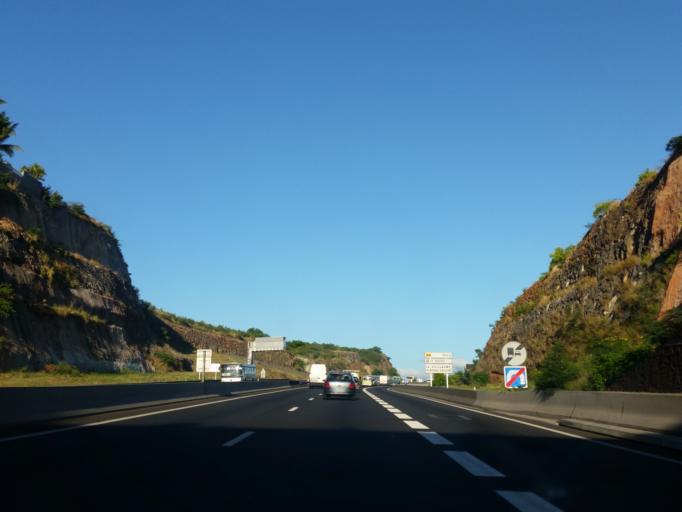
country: RE
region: Reunion
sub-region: Reunion
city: Saint-Paul
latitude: -21.0169
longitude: 55.2626
